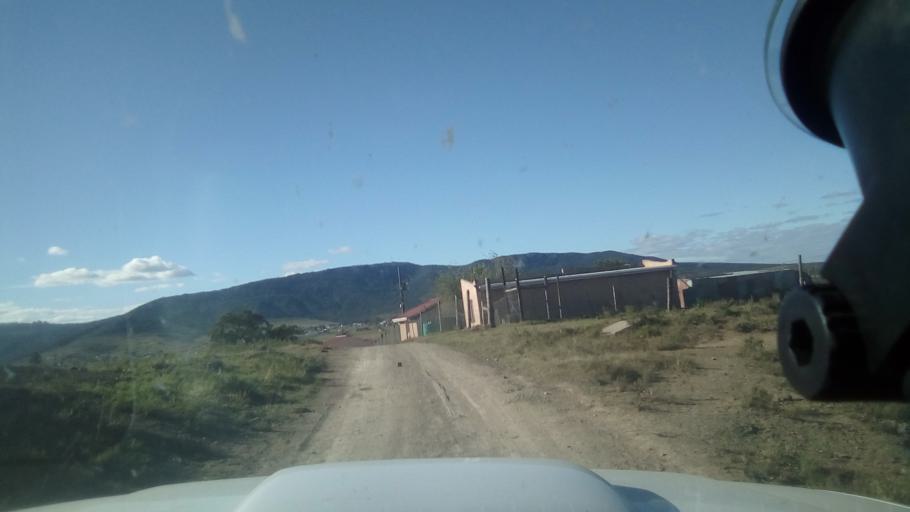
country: ZA
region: Eastern Cape
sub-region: Buffalo City Metropolitan Municipality
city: Bhisho
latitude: -32.7525
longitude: 27.3541
